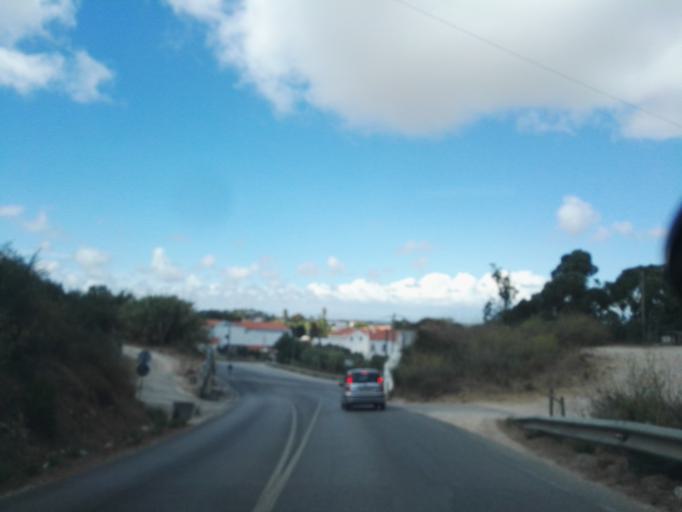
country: PT
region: Setubal
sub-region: Sesimbra
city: Sesimbra
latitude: 38.4635
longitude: -9.0951
